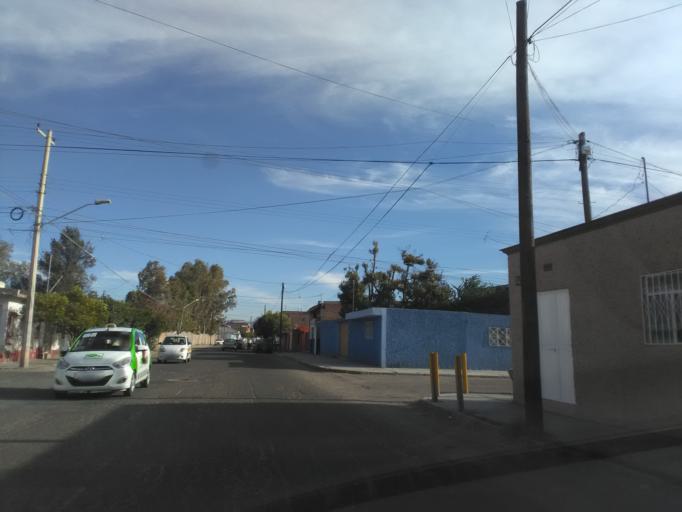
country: MX
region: Durango
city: Victoria de Durango
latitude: 24.0285
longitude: -104.6314
